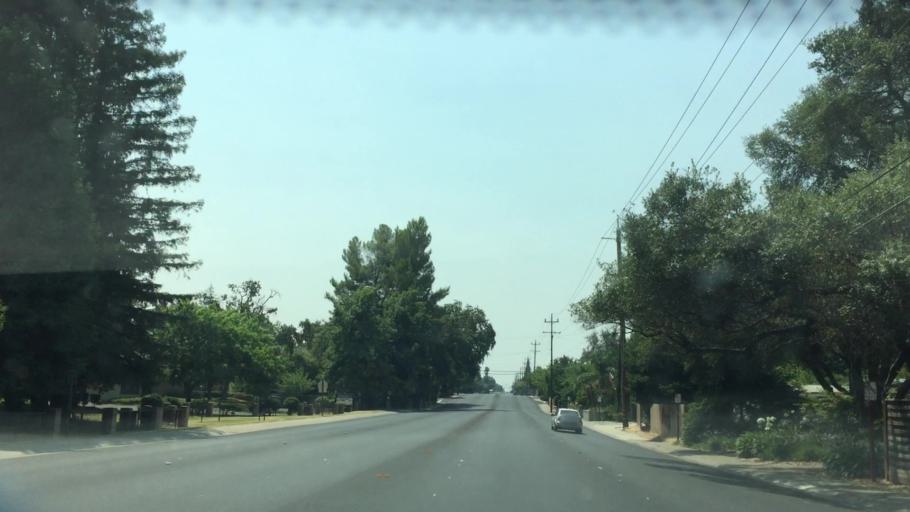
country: US
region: California
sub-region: Sacramento County
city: Arden-Arcade
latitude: 38.6261
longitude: -121.3645
